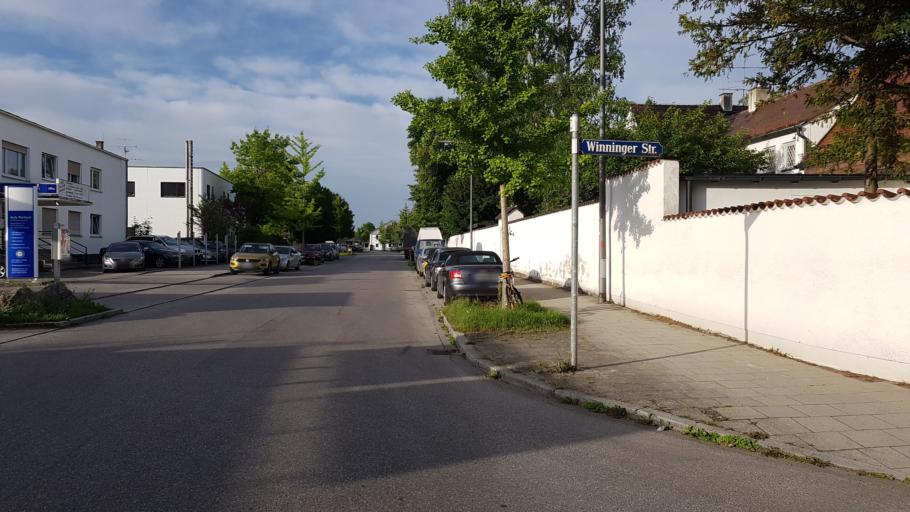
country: DE
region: Bavaria
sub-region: Upper Bavaria
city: Unterhaching
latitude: 48.0900
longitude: 11.6304
